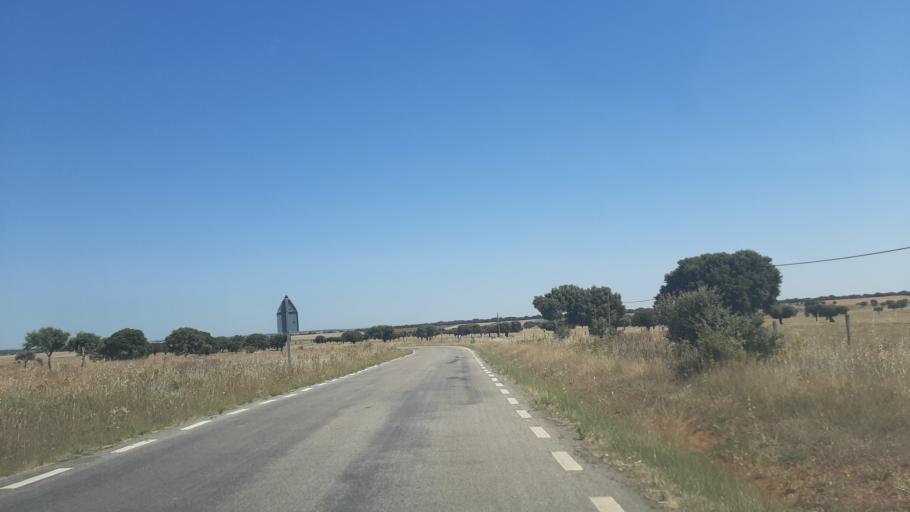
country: ES
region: Castille and Leon
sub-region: Provincia de Salamanca
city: Cabrillas
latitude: 40.7069
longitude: -6.1788
